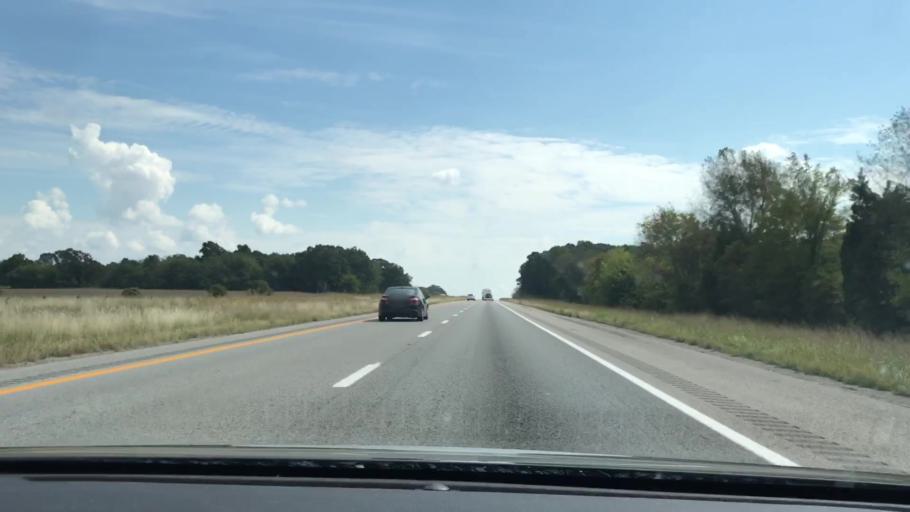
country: US
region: Kentucky
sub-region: Christian County
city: Hopkinsville
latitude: 36.7801
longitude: -87.5728
